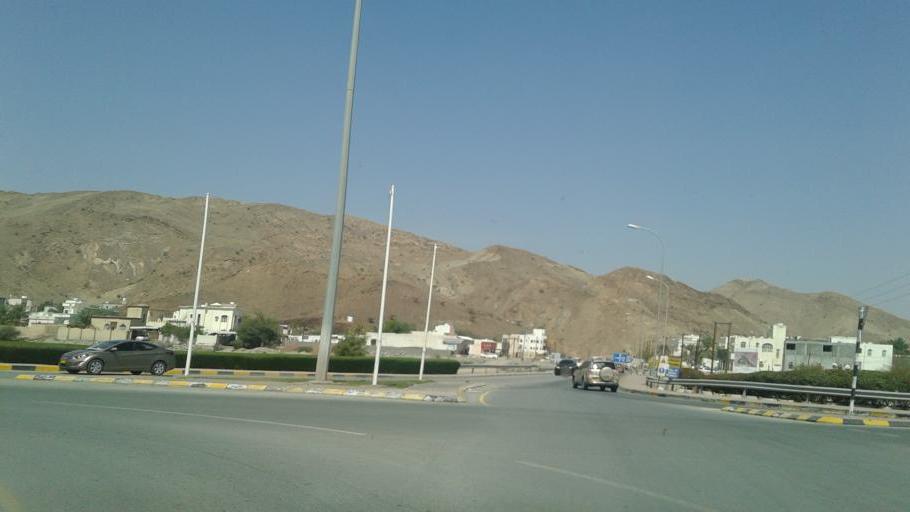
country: OM
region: Al Batinah
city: Rustaq
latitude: 23.4041
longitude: 57.4211
